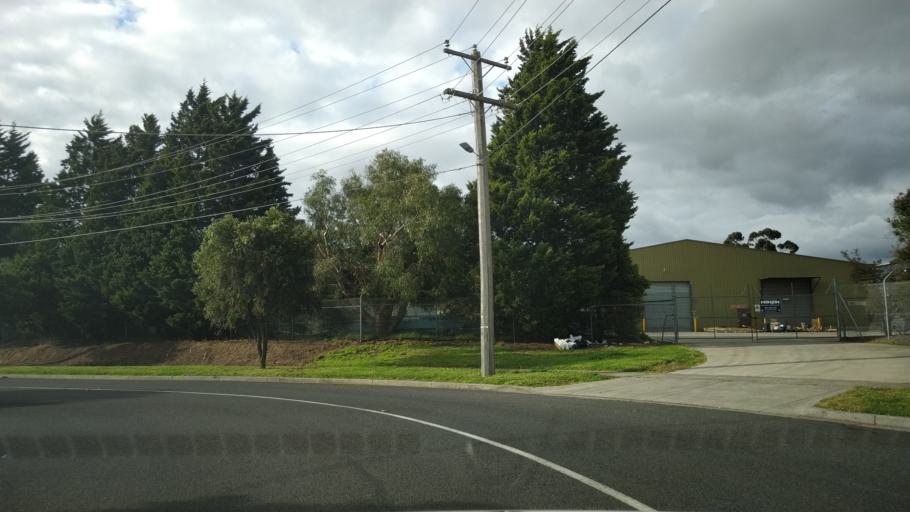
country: AU
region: Victoria
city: Highett
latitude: -37.9496
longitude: 145.0633
